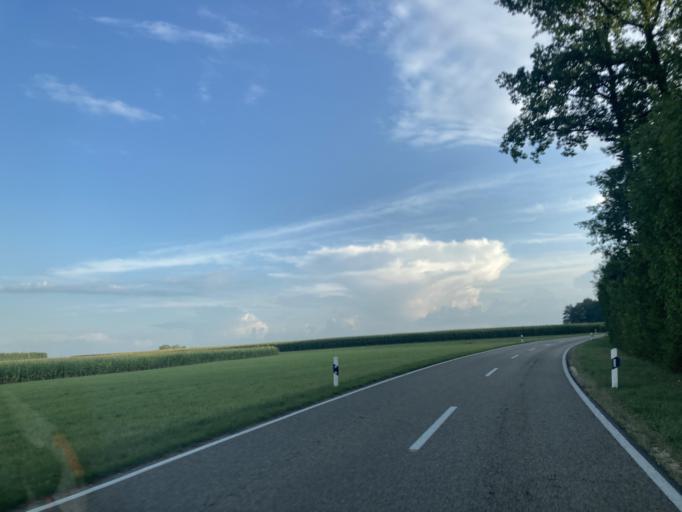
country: DE
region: Bavaria
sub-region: Swabia
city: Medlingen
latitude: 48.5863
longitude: 10.3090
